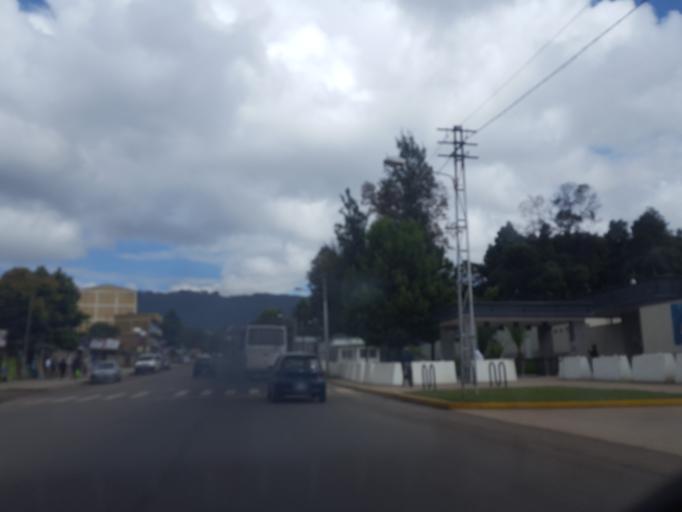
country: ET
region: Adis Abeba
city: Addis Ababa
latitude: 9.0583
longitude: 38.7625
